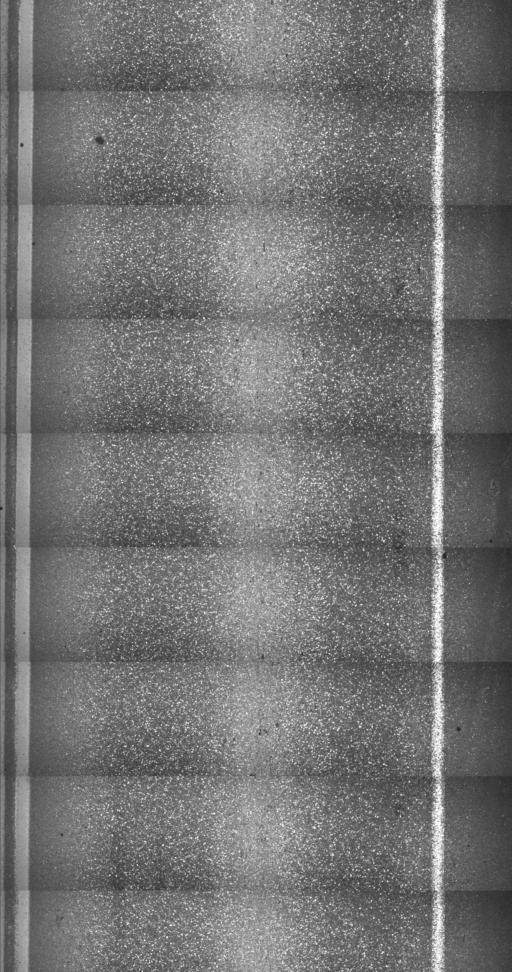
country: US
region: Vermont
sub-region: Chittenden County
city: Essex Junction
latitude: 44.4710
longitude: -73.1131
